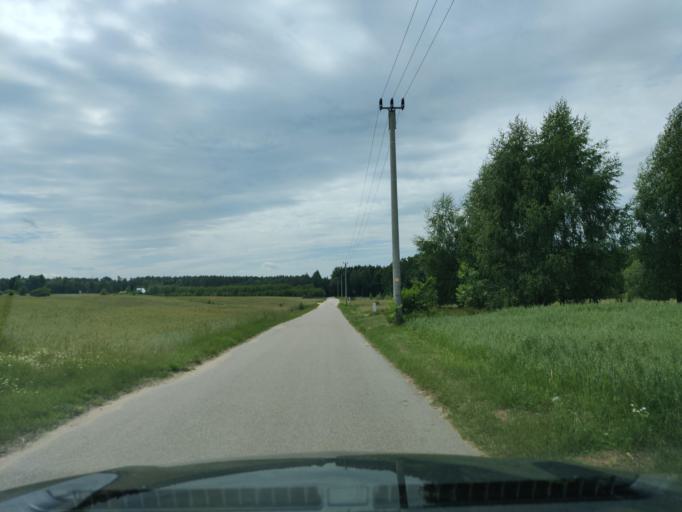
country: PL
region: Masovian Voivodeship
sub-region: Powiat pultuski
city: Obryte
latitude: 52.7482
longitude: 21.1954
